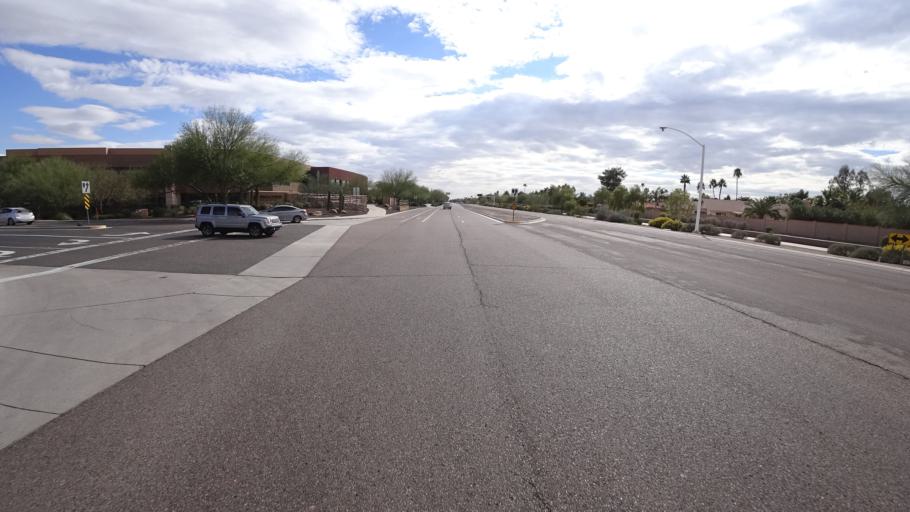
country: US
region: Arizona
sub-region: Maricopa County
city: Scottsdale
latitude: 33.5603
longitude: -111.8913
